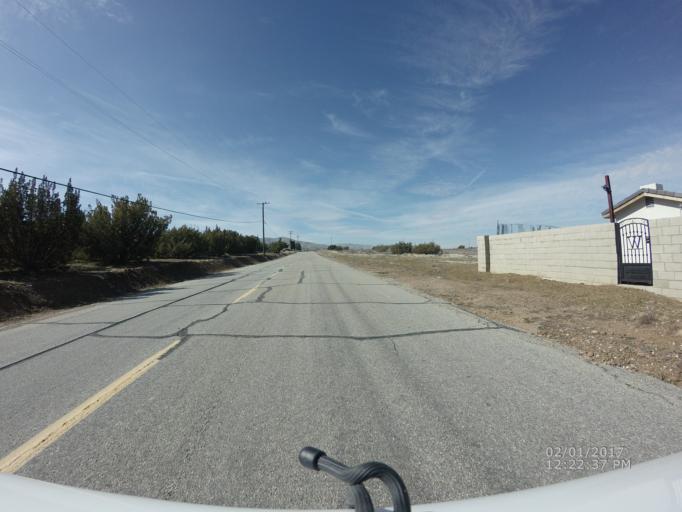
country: US
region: California
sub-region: Los Angeles County
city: Palmdale
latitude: 34.5531
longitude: -118.1333
